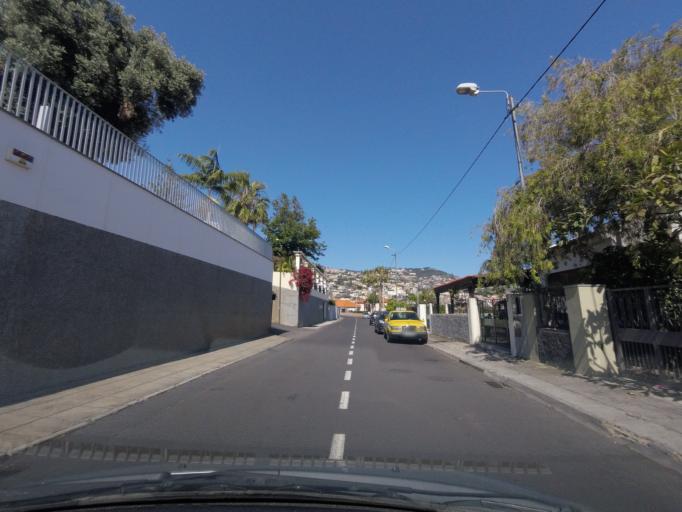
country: PT
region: Madeira
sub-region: Funchal
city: Nossa Senhora do Monte
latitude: 32.6571
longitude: -16.9064
